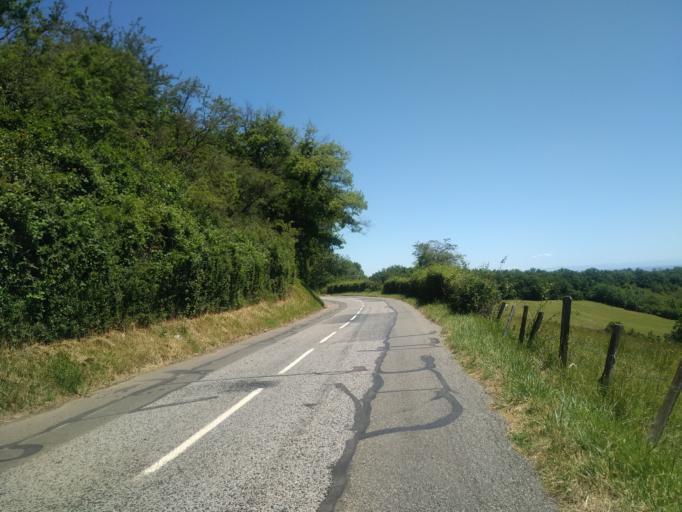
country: FR
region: Rhone-Alpes
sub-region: Departement du Rhone
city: Limonest
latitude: 45.8388
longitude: 4.7959
